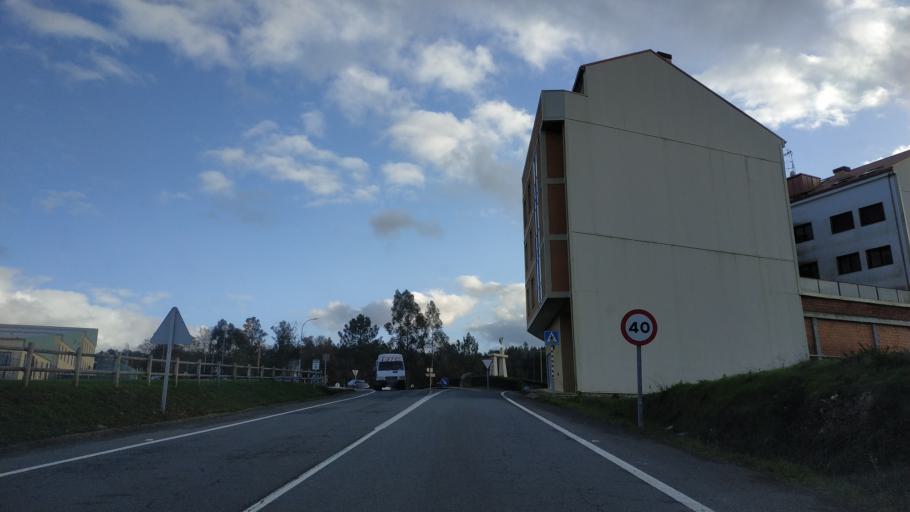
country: ES
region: Galicia
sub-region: Provincia de Pontevedra
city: Silleda
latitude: 42.7933
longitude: -8.1615
